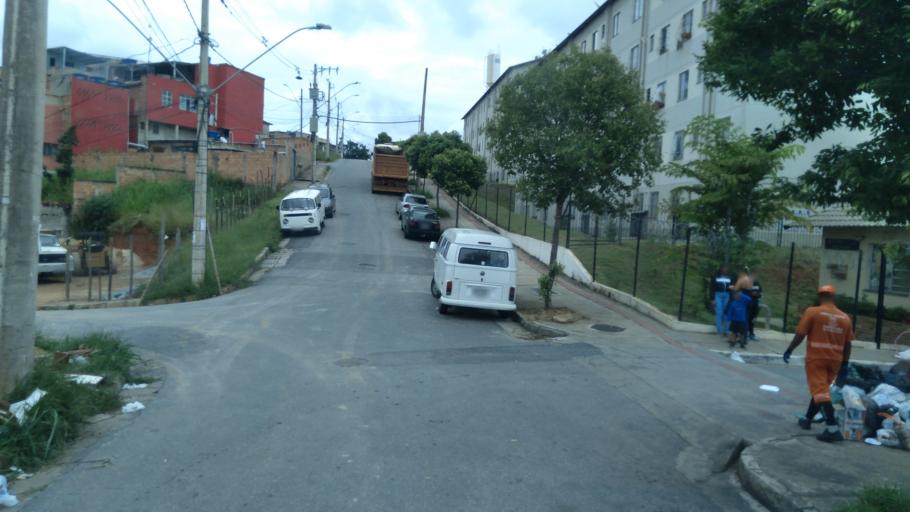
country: BR
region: Minas Gerais
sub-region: Santa Luzia
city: Santa Luzia
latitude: -19.8466
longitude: -43.8902
